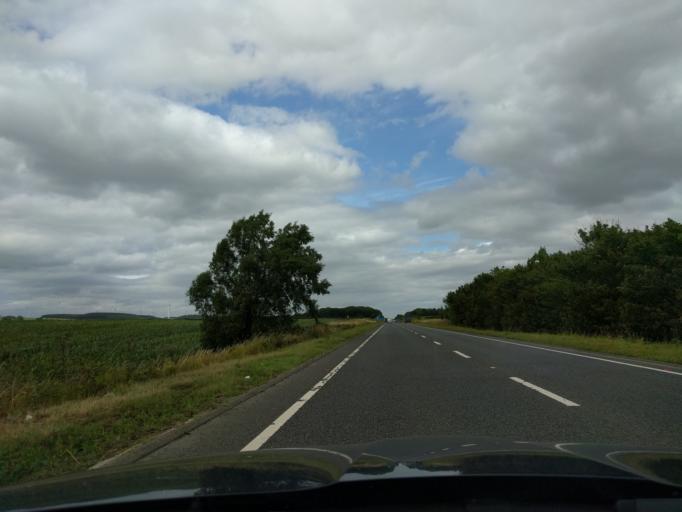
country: GB
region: England
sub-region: Northumberland
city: Ellingham
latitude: 55.4686
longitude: -1.7148
